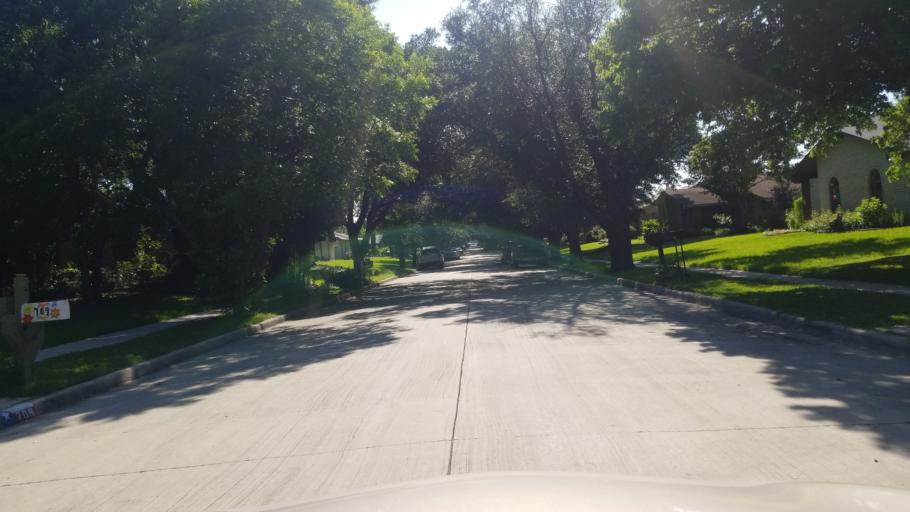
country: US
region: Texas
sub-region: Dallas County
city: Grand Prairie
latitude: 32.6826
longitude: -97.0130
